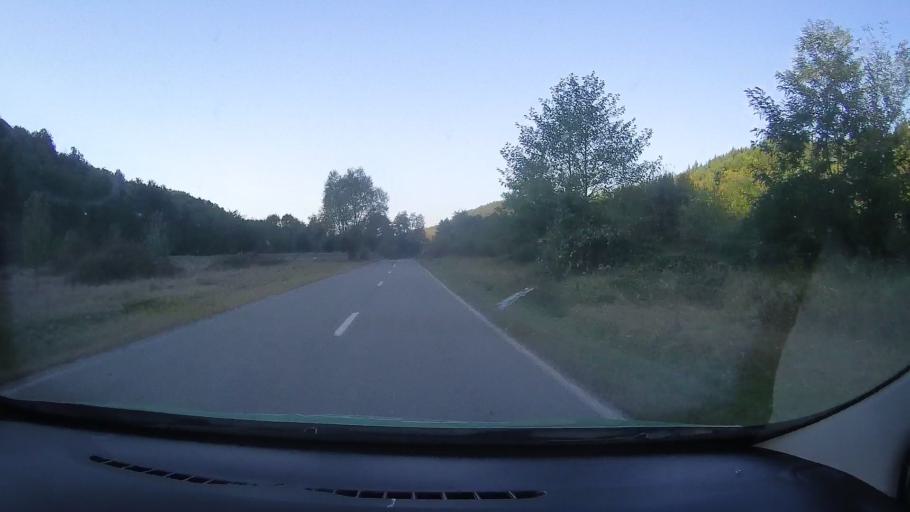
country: RO
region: Timis
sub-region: Comuna Fardea
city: Fardea
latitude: 45.7037
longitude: 22.1604
